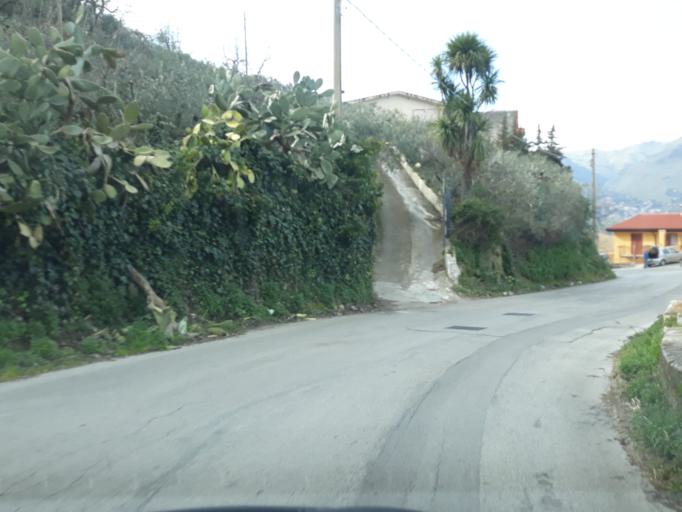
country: IT
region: Sicily
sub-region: Palermo
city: Altofonte
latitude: 38.0410
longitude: 13.3005
